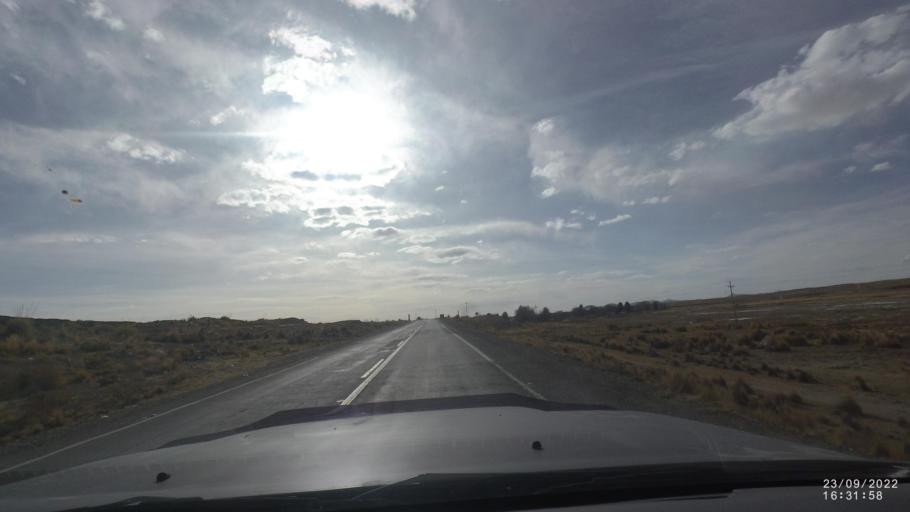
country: BO
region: Oruro
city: Machacamarca
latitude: -18.1649
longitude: -66.9987
